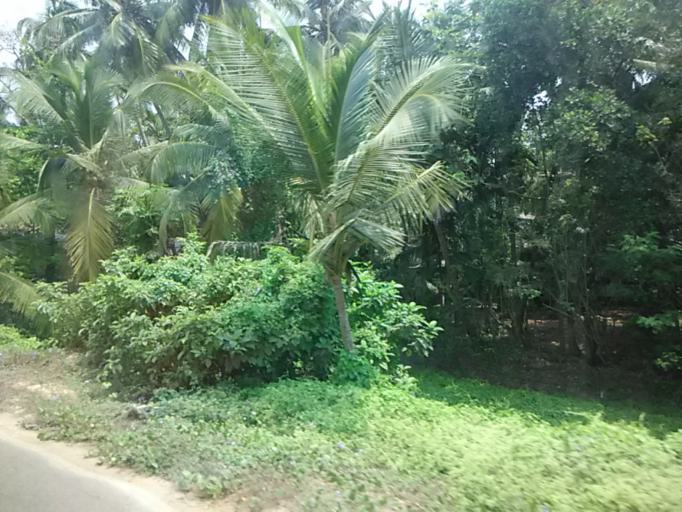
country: IN
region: Kerala
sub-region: Kozhikode
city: Kozhikode
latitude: 11.3248
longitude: 75.7644
